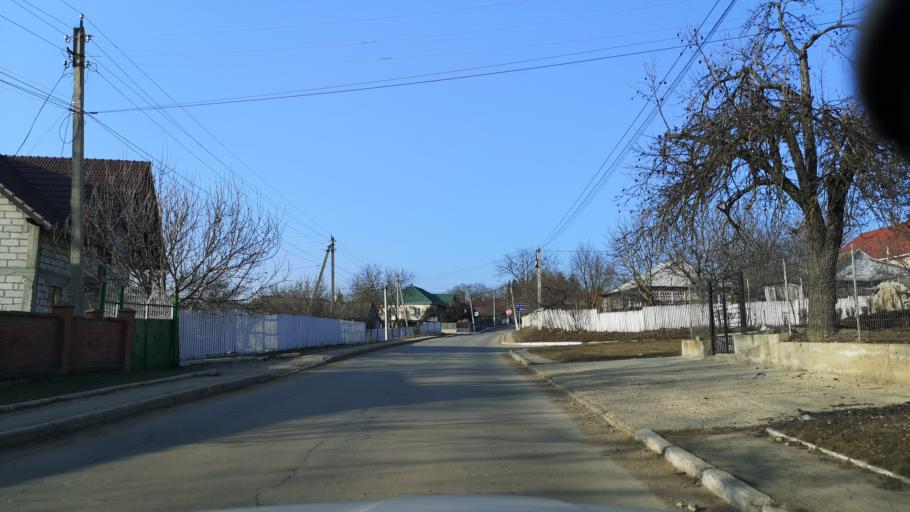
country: MD
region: Stinga Nistrului
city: Bucovat
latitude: 47.1147
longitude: 28.5074
